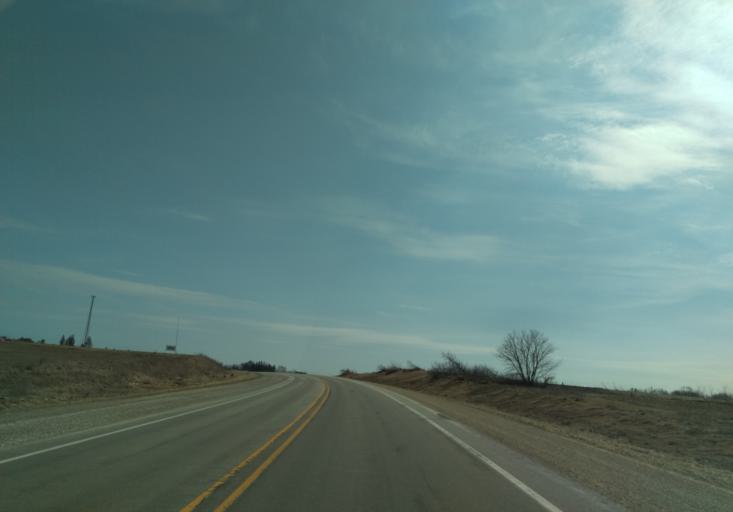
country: US
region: Iowa
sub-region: Winneshiek County
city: Decorah
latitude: 43.4550
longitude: -91.8690
